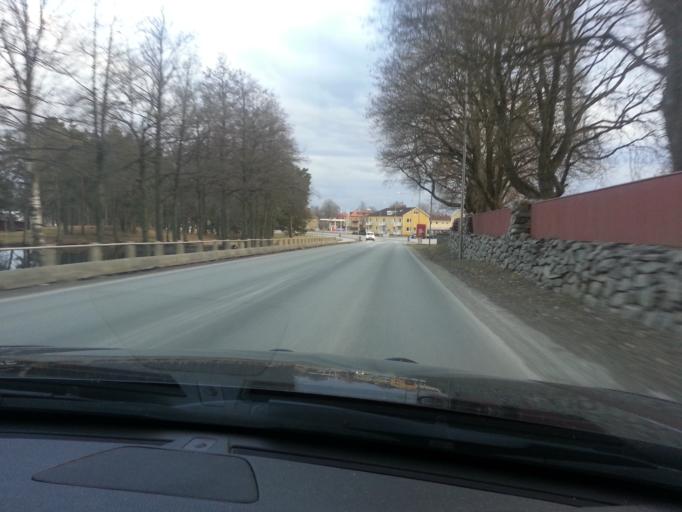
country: SE
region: Joenkoeping
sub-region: Vetlanda Kommun
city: Vetlanda
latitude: 57.4359
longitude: 15.0695
